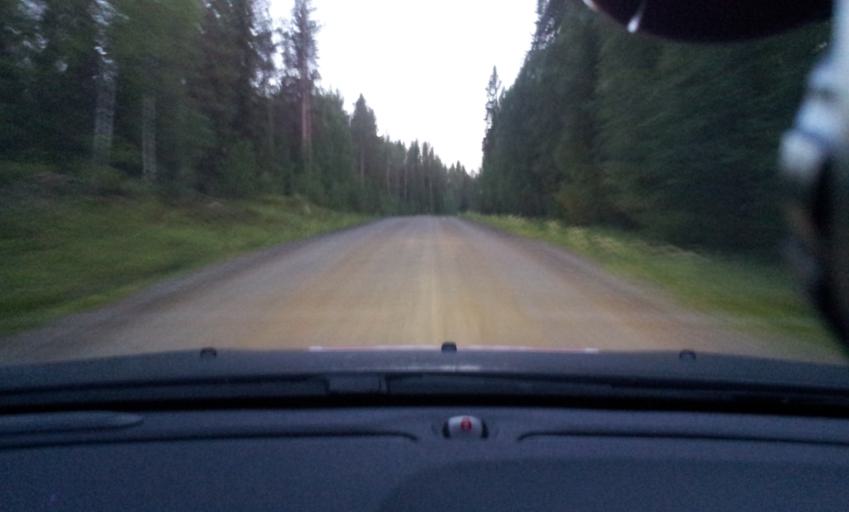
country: SE
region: Vaesternorrland
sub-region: Ange Kommun
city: Ange
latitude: 62.7707
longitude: 15.8982
